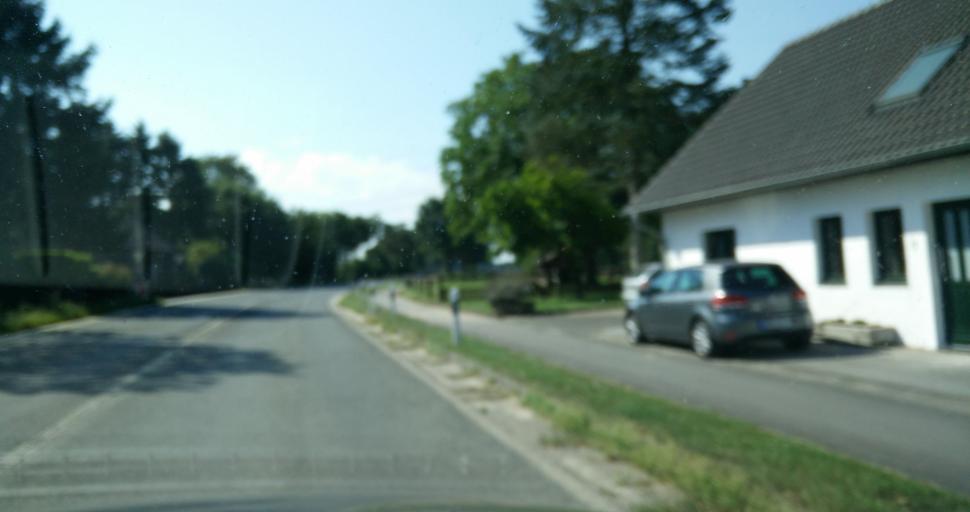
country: DE
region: North Rhine-Westphalia
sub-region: Regierungsbezirk Dusseldorf
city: Hochfeld
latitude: 51.3341
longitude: 6.7490
